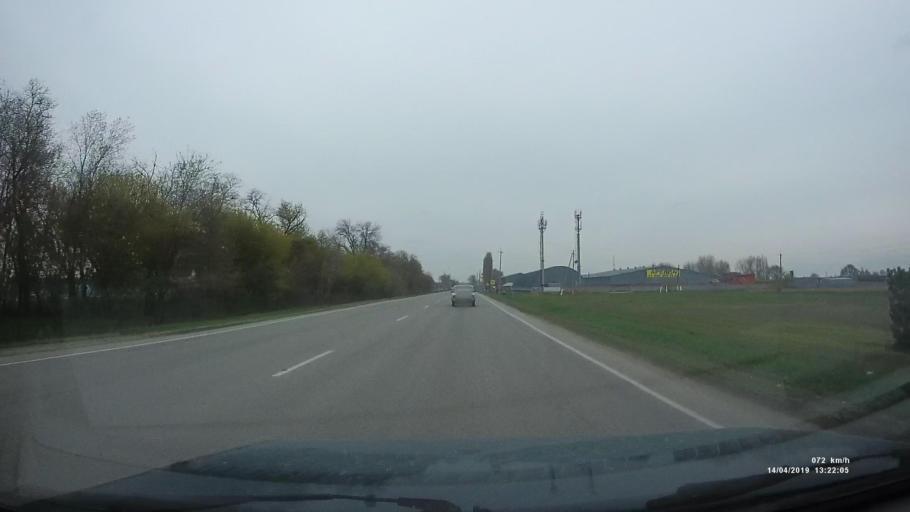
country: RU
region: Rostov
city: Kuleshovka
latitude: 47.0824
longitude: 39.5151
